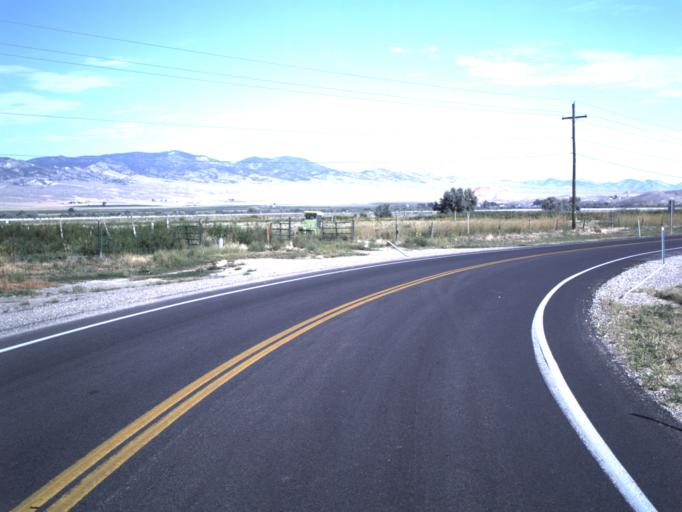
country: US
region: Utah
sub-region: Sevier County
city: Salina
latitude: 38.9741
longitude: -111.8601
